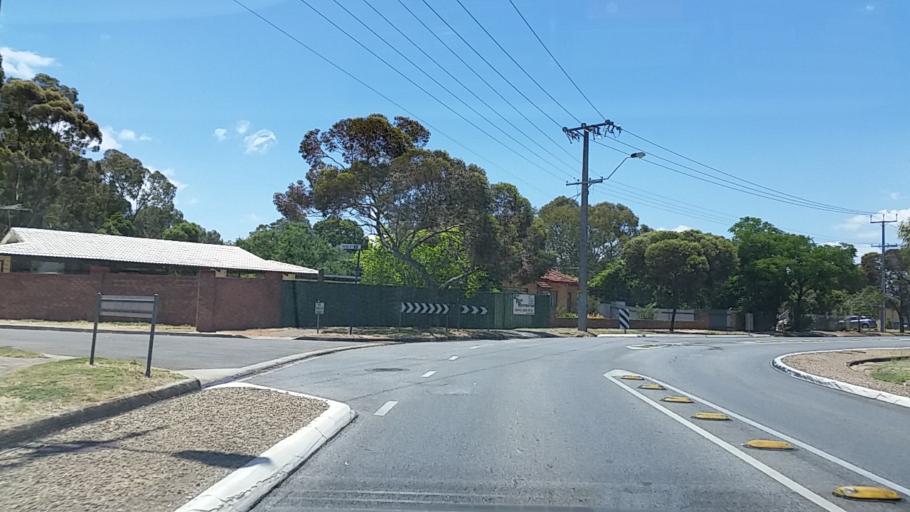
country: AU
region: South Australia
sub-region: Salisbury
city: Salisbury
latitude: -34.7631
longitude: 138.6300
